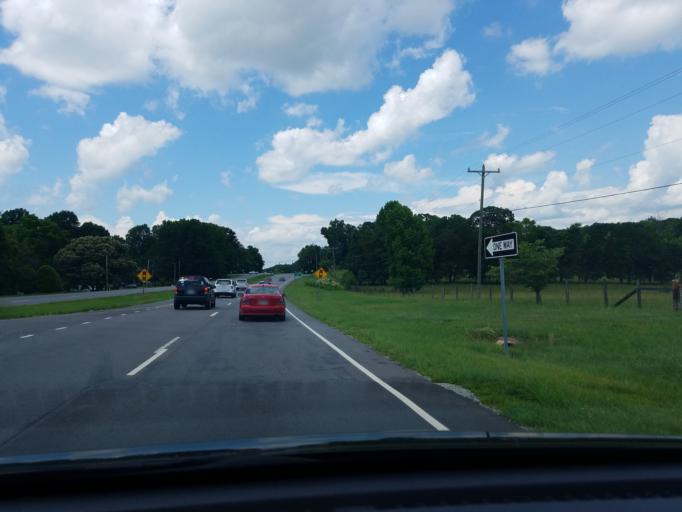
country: US
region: North Carolina
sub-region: Durham County
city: Gorman
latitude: 36.1147
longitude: -78.9045
